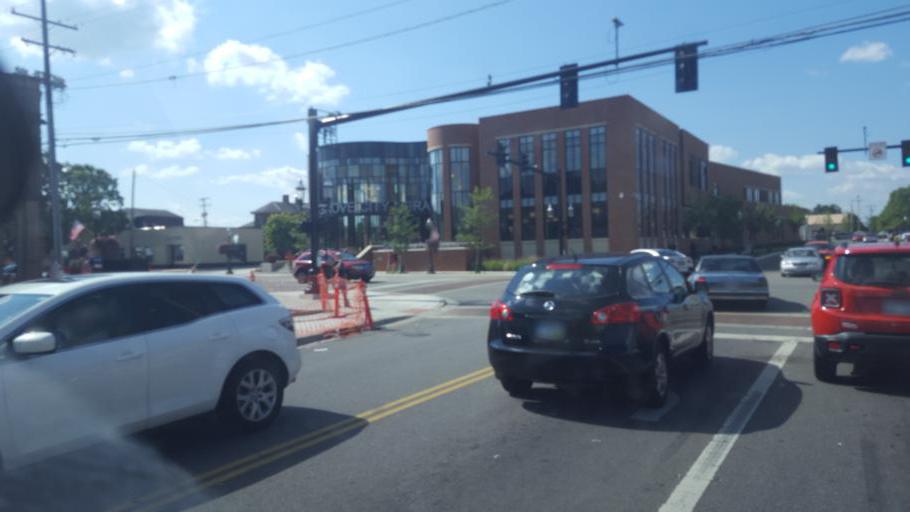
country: US
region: Ohio
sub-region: Franklin County
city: Grove City
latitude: 39.8835
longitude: -83.0922
